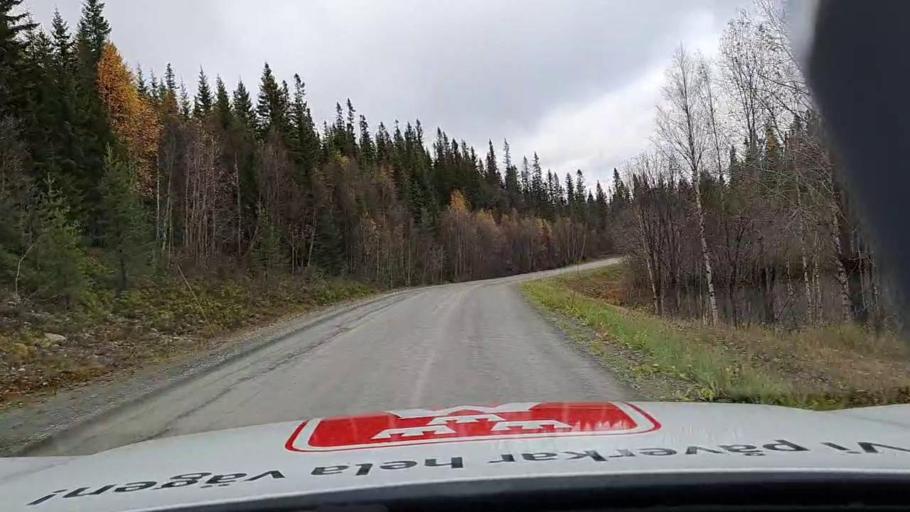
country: SE
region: Jaemtland
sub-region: Krokoms Kommun
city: Valla
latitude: 63.0459
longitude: 13.9593
